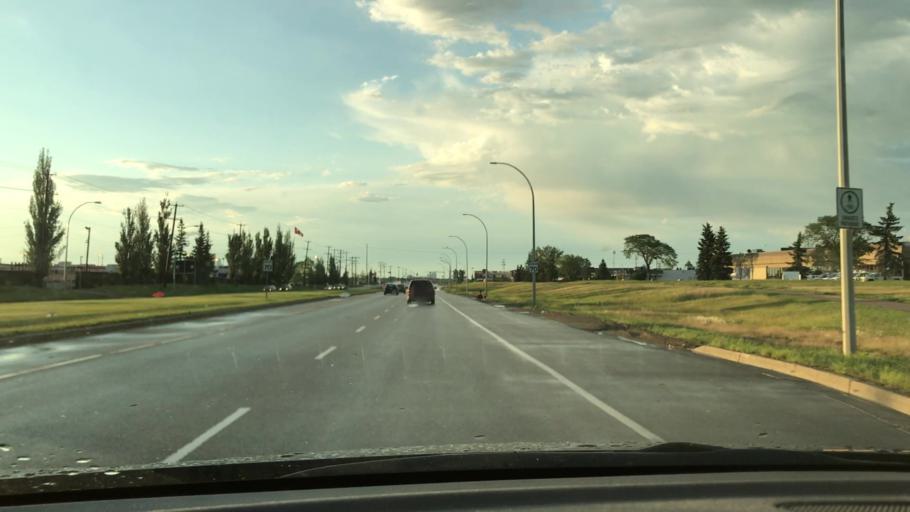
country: CA
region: Alberta
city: Edmonton
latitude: 53.4843
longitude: -113.4668
